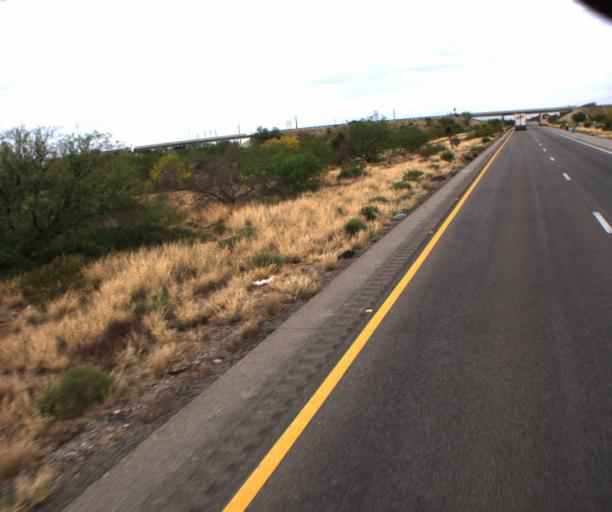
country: US
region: Arizona
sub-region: Pima County
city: Vail
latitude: 32.0267
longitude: -110.7181
